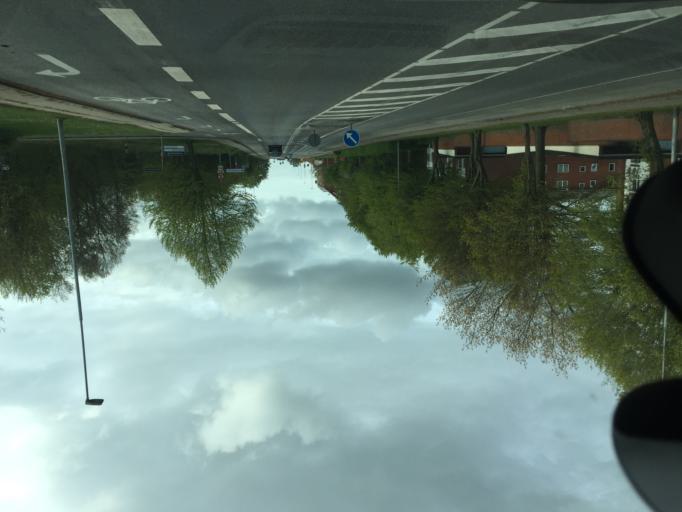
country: DK
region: South Denmark
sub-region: Odense Kommune
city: Odense
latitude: 55.4022
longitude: 10.3399
